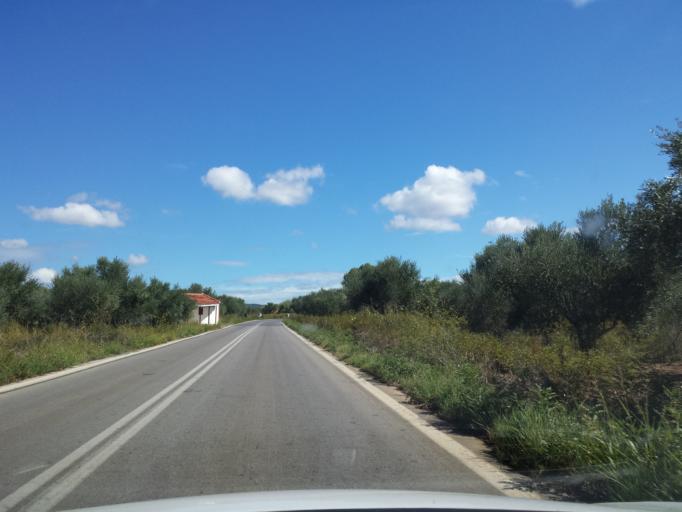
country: GR
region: Peloponnese
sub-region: Nomos Messinias
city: Pylos
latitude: 36.9544
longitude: 21.7648
